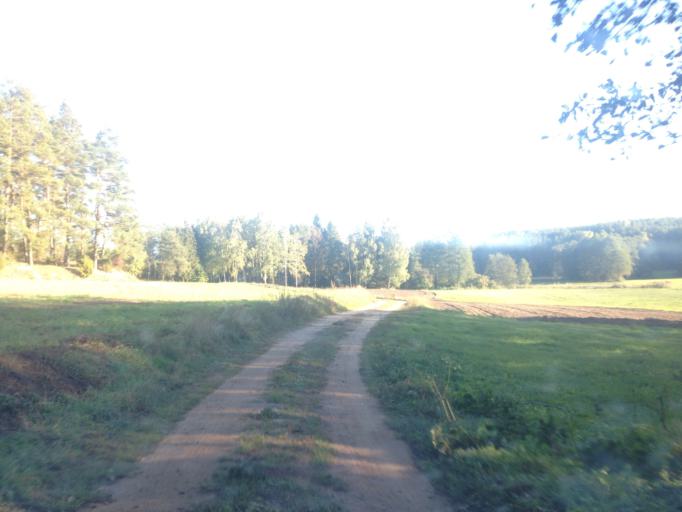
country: PL
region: Kujawsko-Pomorskie
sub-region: Powiat brodnicki
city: Bartniczka
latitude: 53.2767
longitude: 19.6228
